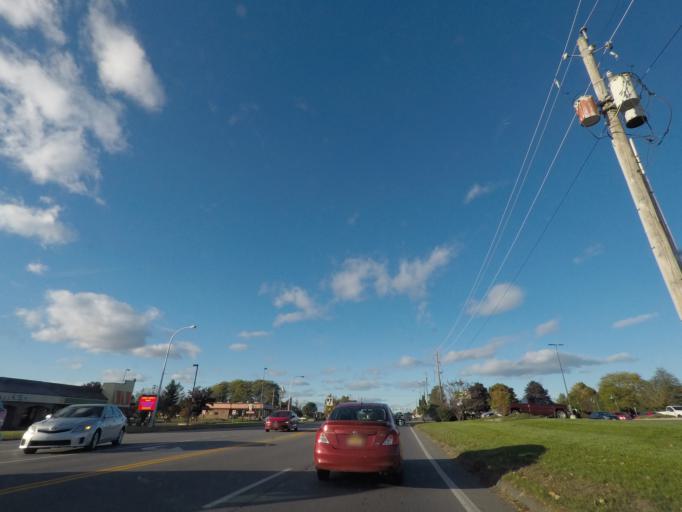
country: US
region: New York
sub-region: Saratoga County
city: Country Knolls
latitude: 42.8607
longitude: -73.7808
